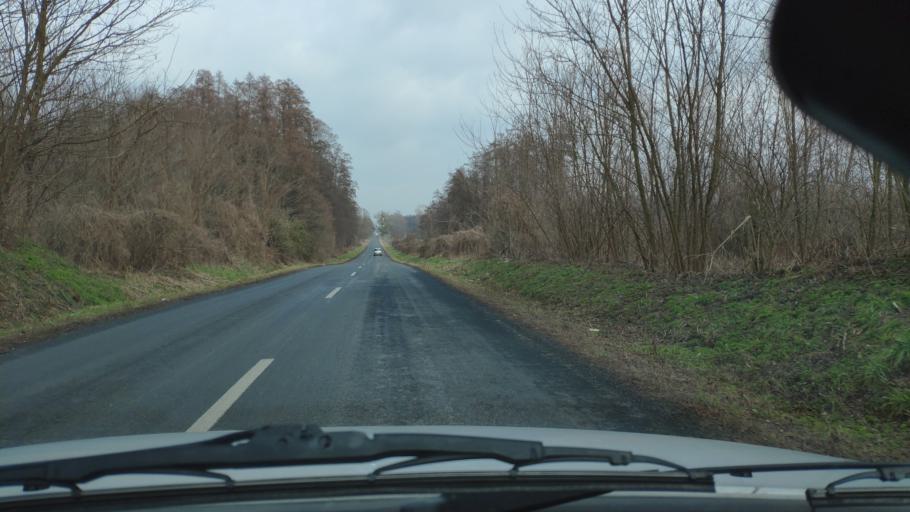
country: HU
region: Zala
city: Nagykanizsa
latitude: 46.4425
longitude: 16.9247
